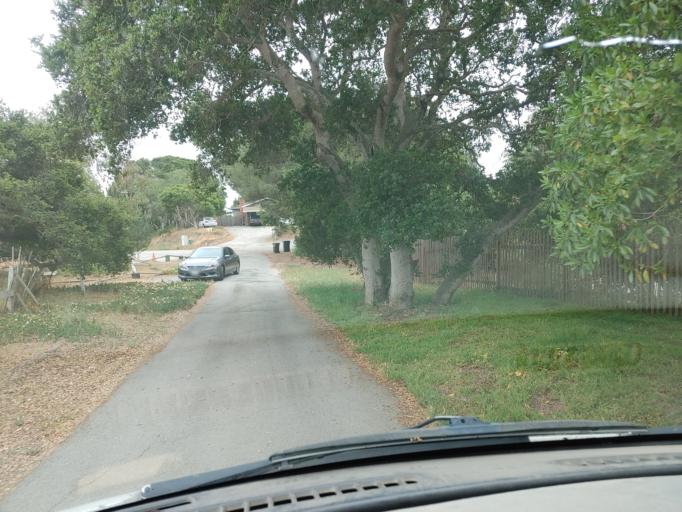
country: US
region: California
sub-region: Monterey County
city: Prunedale
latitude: 36.7924
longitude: -121.6864
